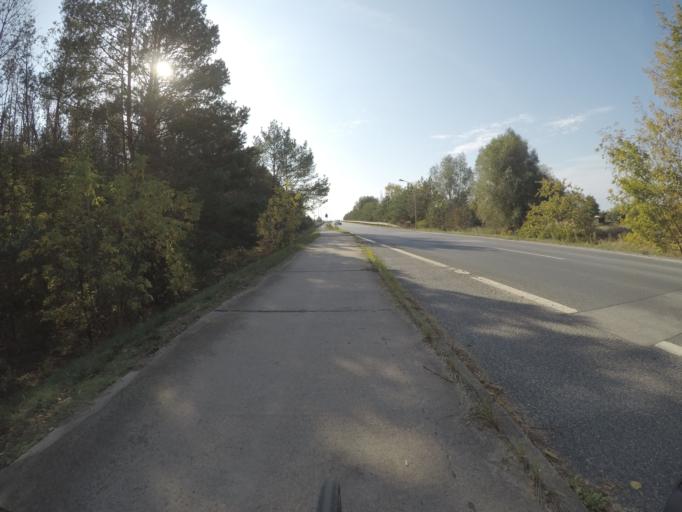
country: DE
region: Brandenburg
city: Leegebruch
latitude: 52.6978
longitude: 13.2055
